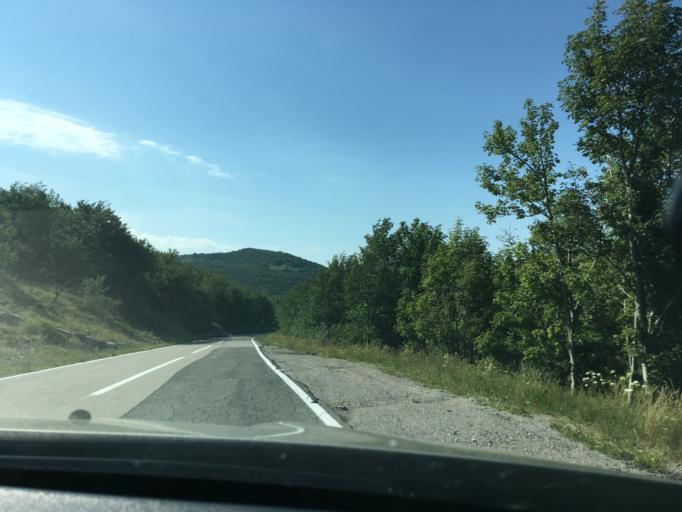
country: HR
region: Primorsko-Goranska
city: Krasica
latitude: 45.3602
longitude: 14.6159
